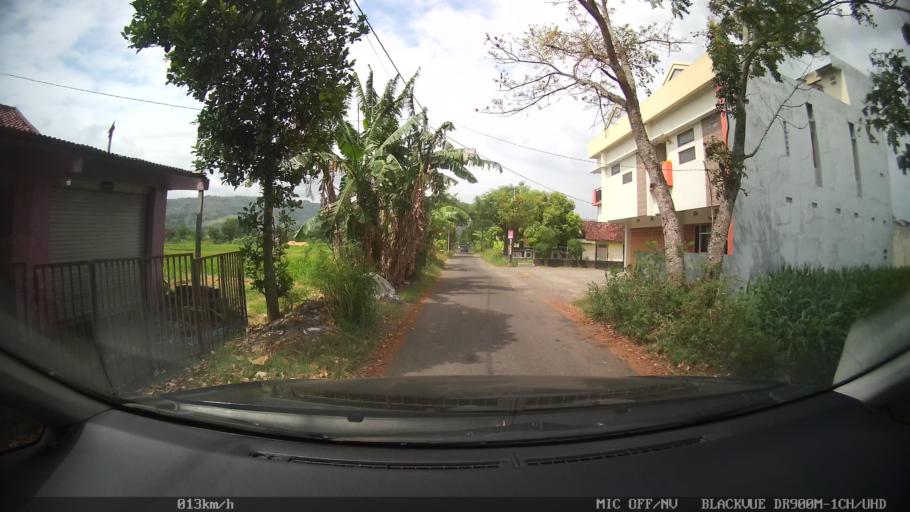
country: ID
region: Daerah Istimewa Yogyakarta
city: Depok
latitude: -7.8288
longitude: 110.4634
